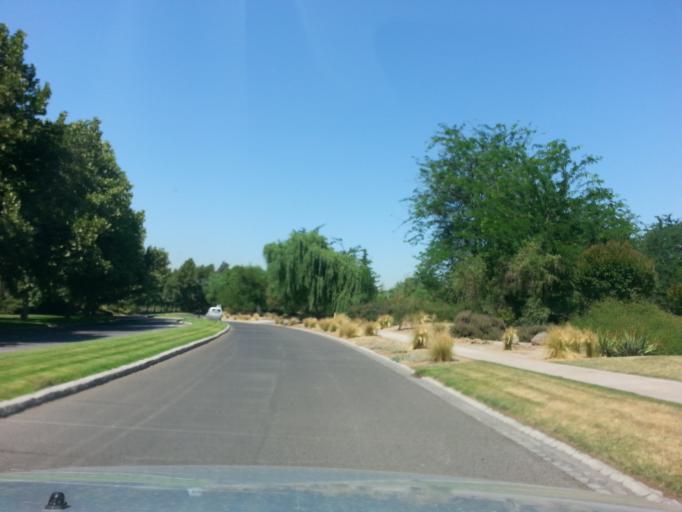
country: CL
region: Santiago Metropolitan
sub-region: Provincia de Chacabuco
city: Chicureo Abajo
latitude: -33.2375
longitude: -70.6738
